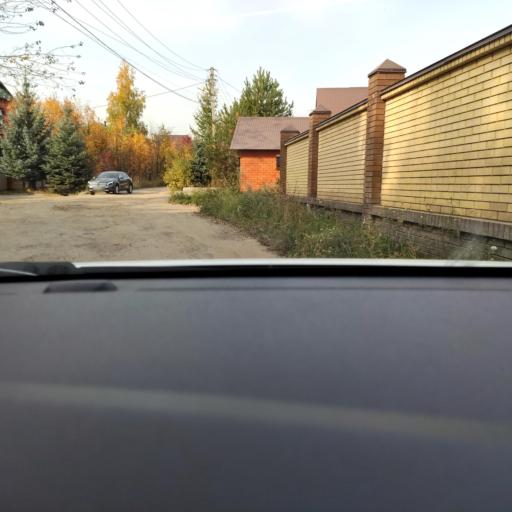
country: RU
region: Tatarstan
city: Vysokaya Gora
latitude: 55.8069
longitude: 49.2466
